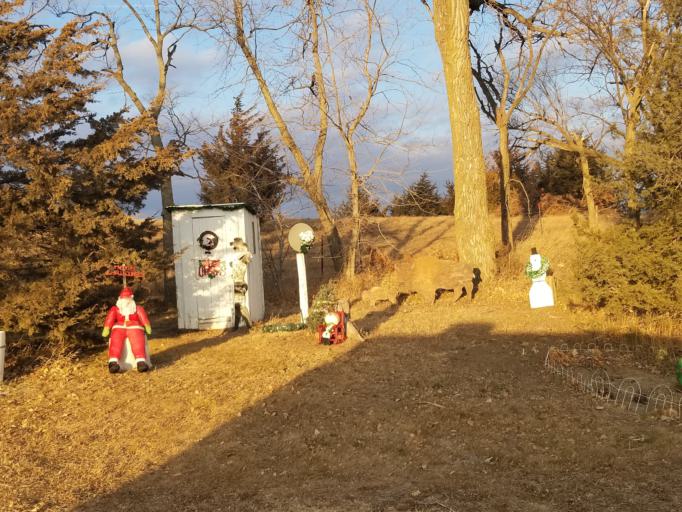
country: US
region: Nebraska
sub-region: Knox County
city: Bloomfield
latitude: 42.5974
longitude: -97.7594
